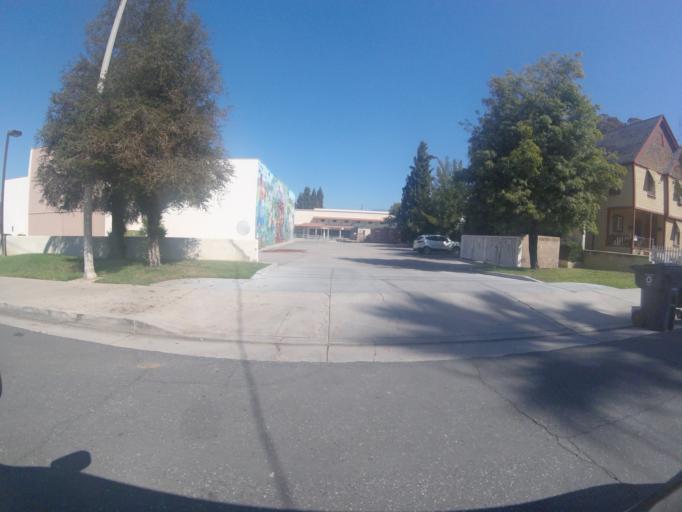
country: US
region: California
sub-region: San Bernardino County
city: Redlands
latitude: 34.0542
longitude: -117.1774
